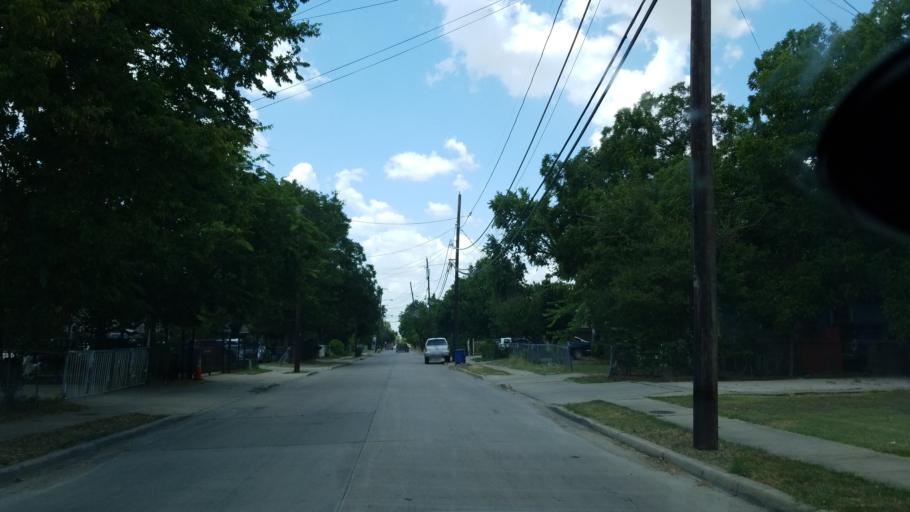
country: US
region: Texas
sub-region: Dallas County
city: Cockrell Hill
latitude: 32.7513
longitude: -96.9128
